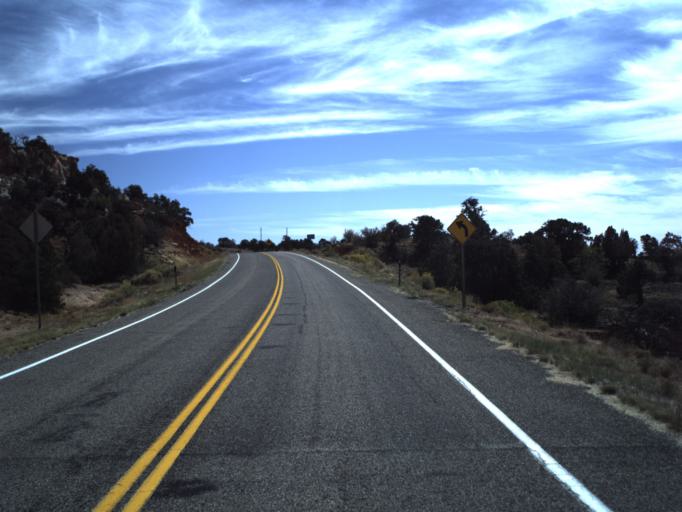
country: US
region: Utah
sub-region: Wayne County
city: Loa
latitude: 37.8905
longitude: -111.4510
